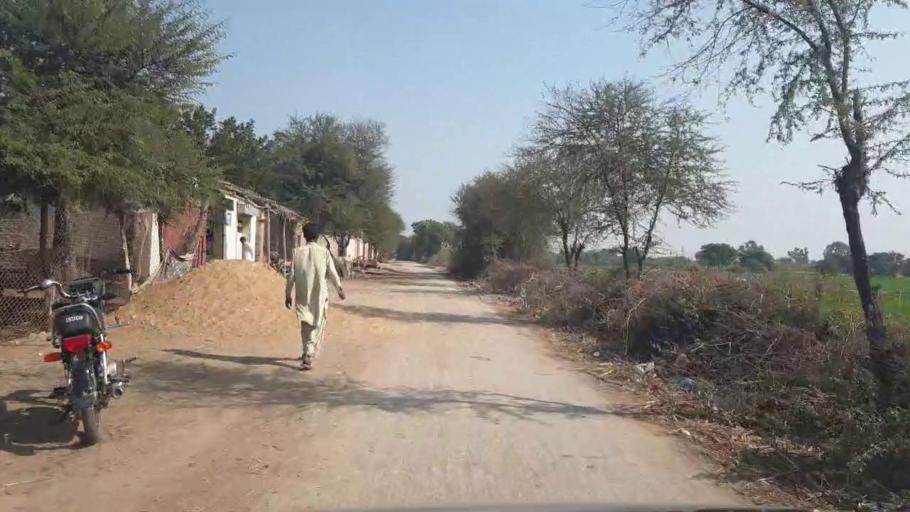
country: PK
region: Sindh
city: Tando Adam
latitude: 25.8202
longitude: 68.6528
